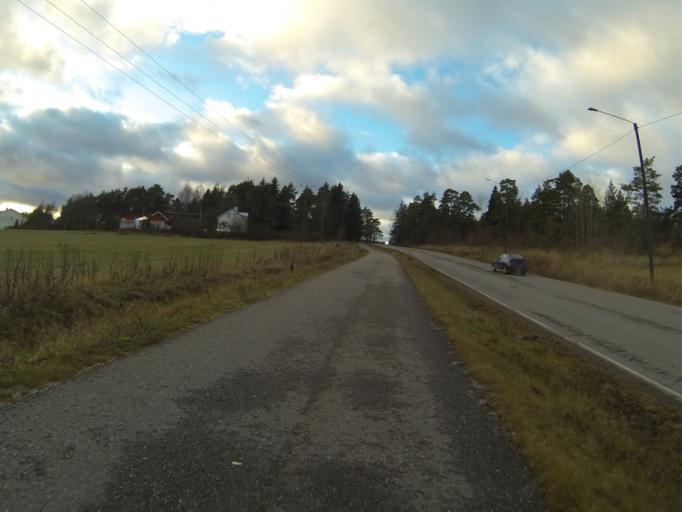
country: FI
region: Varsinais-Suomi
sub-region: Salo
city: Halikko
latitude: 60.3977
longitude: 23.0621
